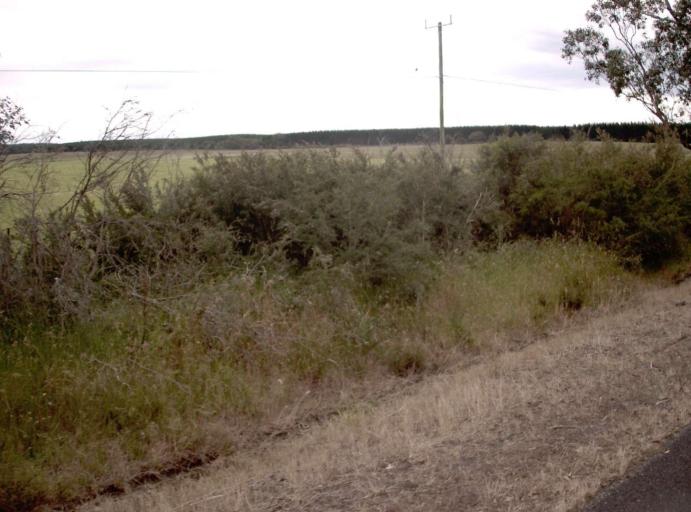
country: AU
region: Victoria
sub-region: Wellington
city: Sale
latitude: -38.2270
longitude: 147.0554
